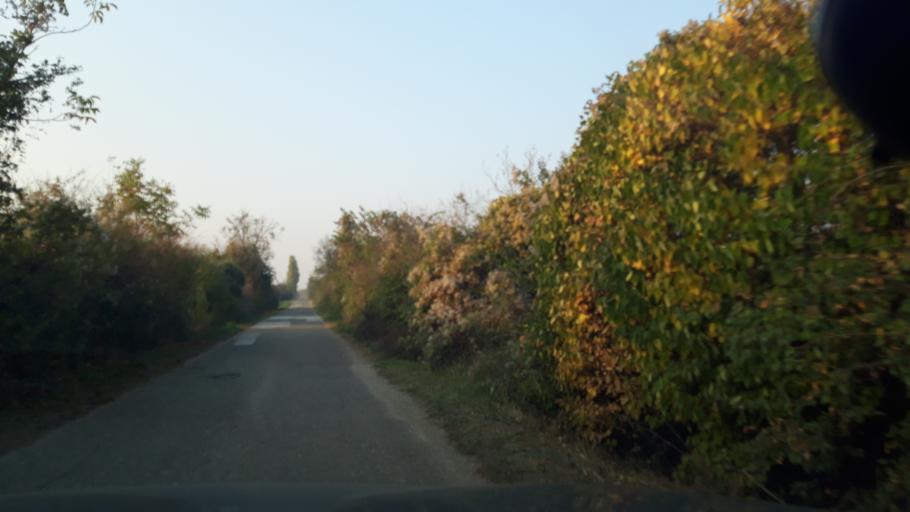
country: RS
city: Cortanovci
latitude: 45.1317
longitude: 19.9881
